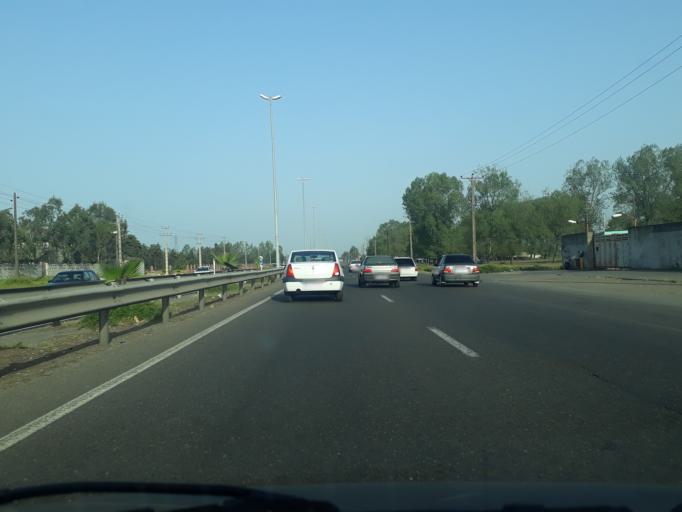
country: IR
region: Gilan
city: Bandar-e Anzali
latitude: 37.4609
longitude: 49.5720
